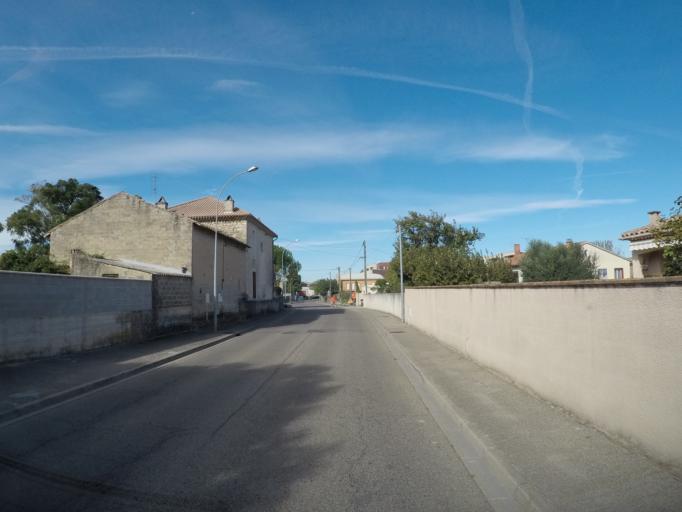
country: FR
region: Provence-Alpes-Cote d'Azur
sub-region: Departement du Vaucluse
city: Bollene
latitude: 44.2843
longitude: 4.7540
